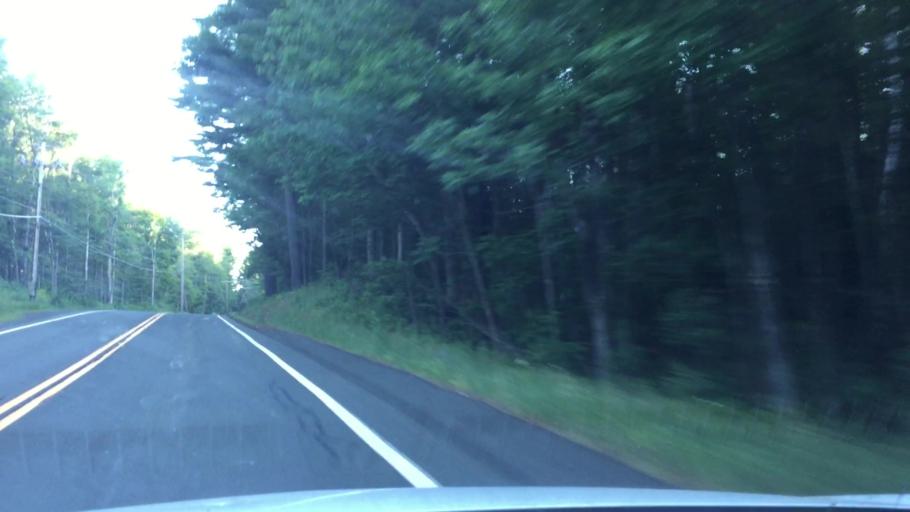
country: US
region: Massachusetts
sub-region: Berkshire County
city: Otis
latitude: 42.2216
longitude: -73.1037
